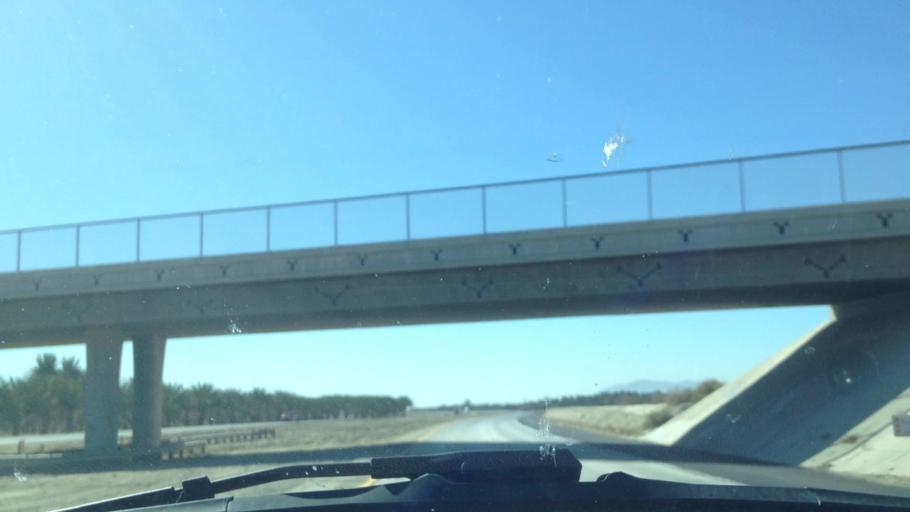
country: US
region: California
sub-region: Riverside County
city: Thermal
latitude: 33.6278
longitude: -116.1228
